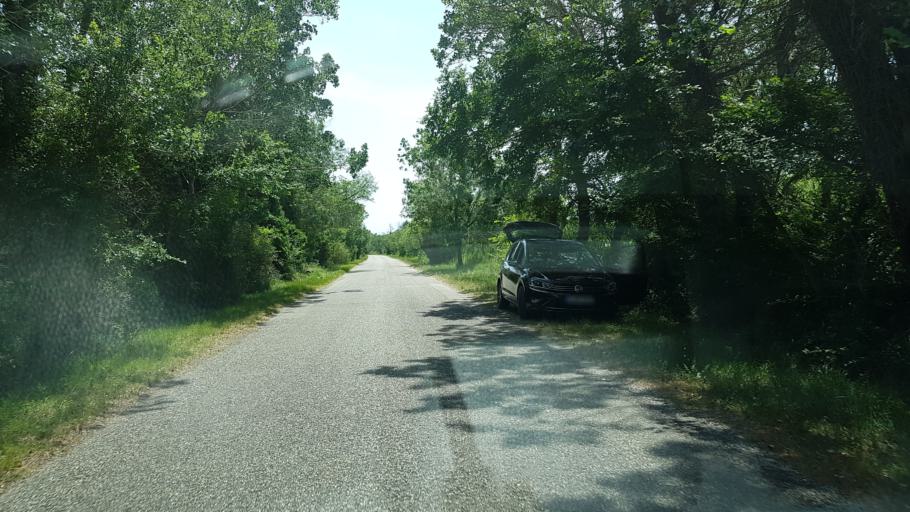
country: FR
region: Provence-Alpes-Cote d'Azur
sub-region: Departement des Bouches-du-Rhone
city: Port-Saint-Louis-du-Rhone
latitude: 43.4601
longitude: 4.6575
